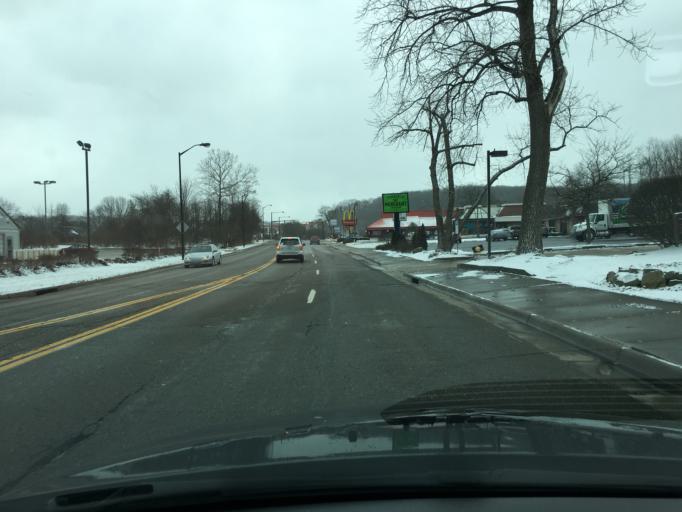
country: US
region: Ohio
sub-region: Summit County
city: Fairlawn
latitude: 41.1356
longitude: -81.5557
